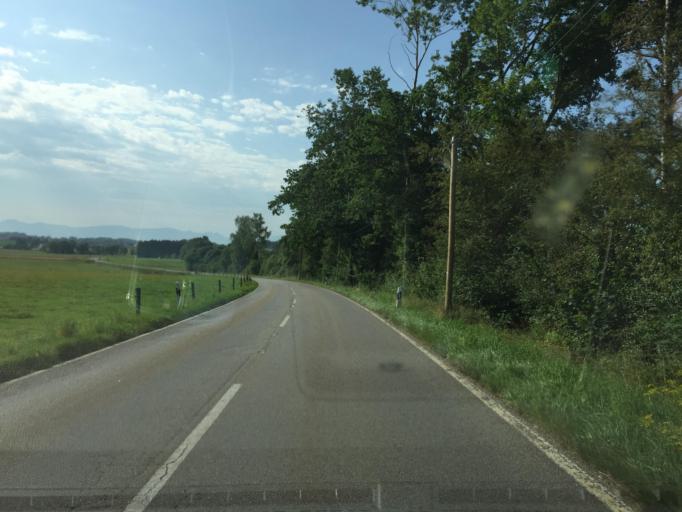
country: DE
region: Bavaria
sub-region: Upper Bavaria
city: Tuntenhausen
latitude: 47.9618
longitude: 12.0131
